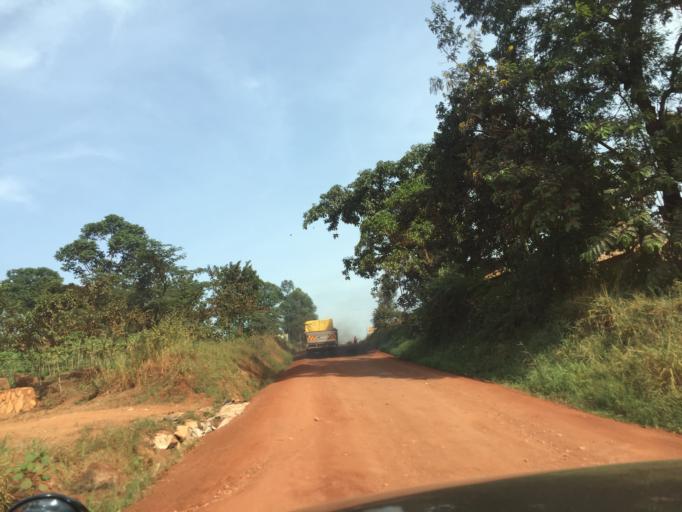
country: UG
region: Central Region
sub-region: Wakiso District
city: Wakiso
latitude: 0.4568
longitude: 32.5630
